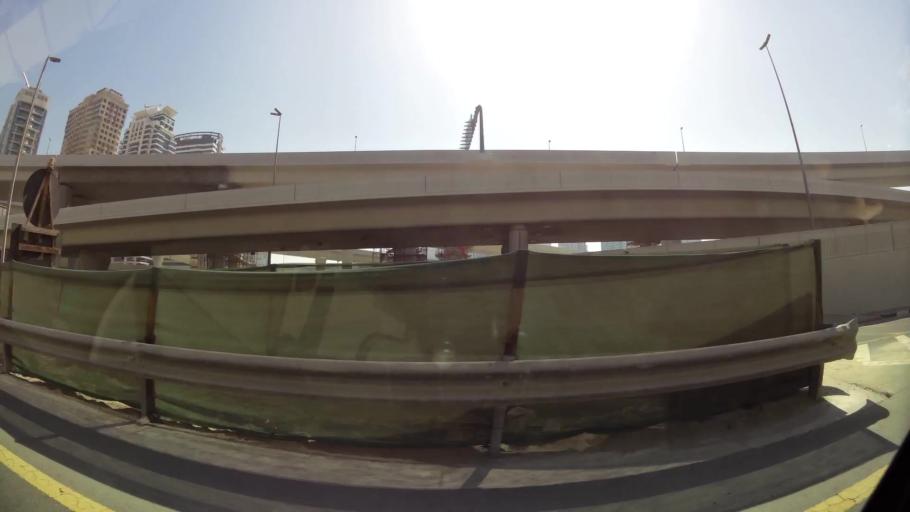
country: AE
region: Dubai
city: Dubai
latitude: 25.0656
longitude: 55.1314
